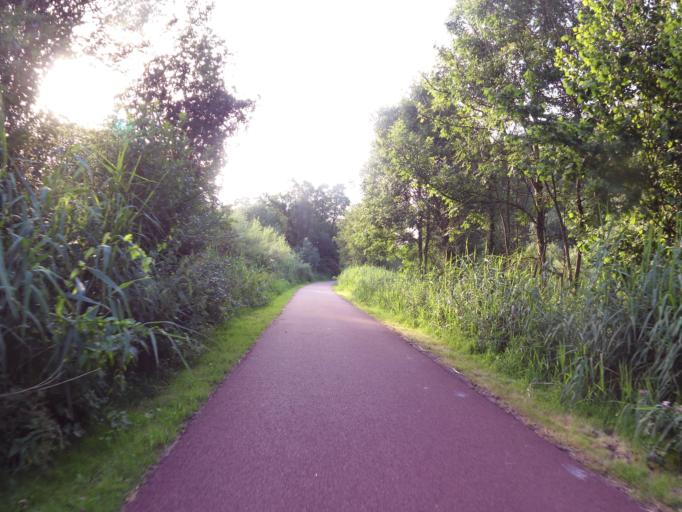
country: NL
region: North Brabant
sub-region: Gemeente Geldrop-Mierlo
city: Geldrop
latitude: 51.4303
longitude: 5.5523
